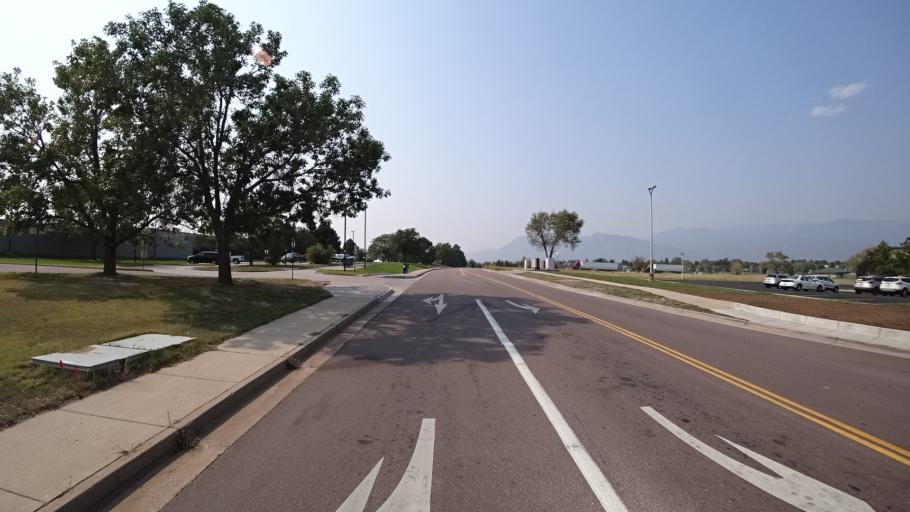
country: US
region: Colorado
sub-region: El Paso County
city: Stratmoor
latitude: 38.8141
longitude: -104.7605
